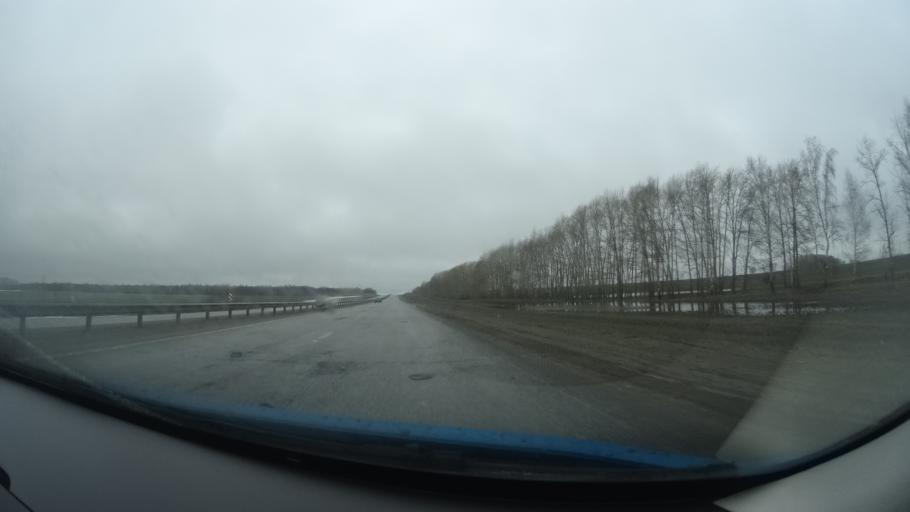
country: RU
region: Bashkortostan
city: Alekseyevka
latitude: 54.7314
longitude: 55.1366
